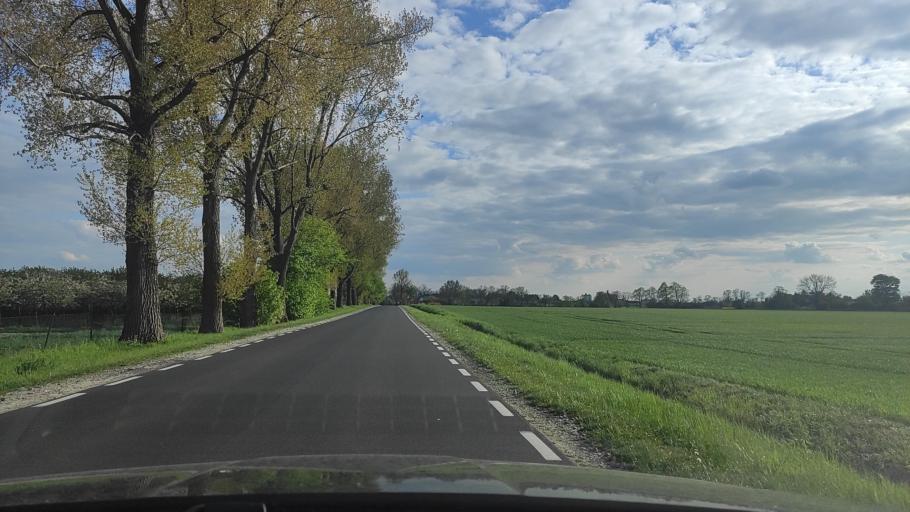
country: PL
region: Greater Poland Voivodeship
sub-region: Powiat poznanski
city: Kostrzyn
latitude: 52.4243
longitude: 17.2285
